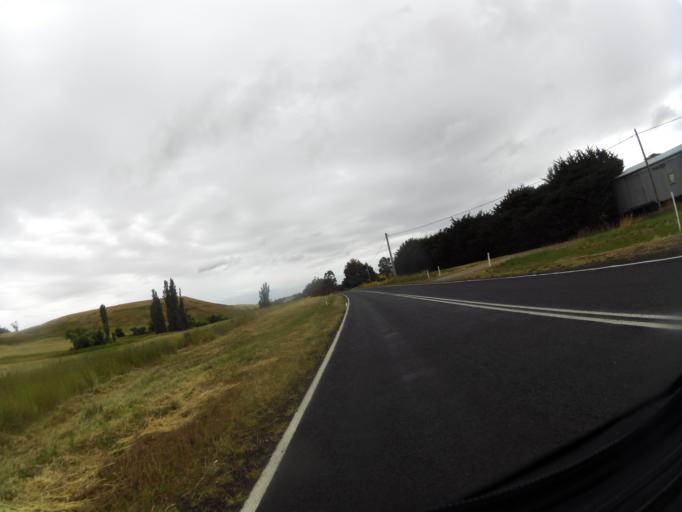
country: AU
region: Victoria
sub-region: Mount Alexander
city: Castlemaine
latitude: -37.1984
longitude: 144.0161
